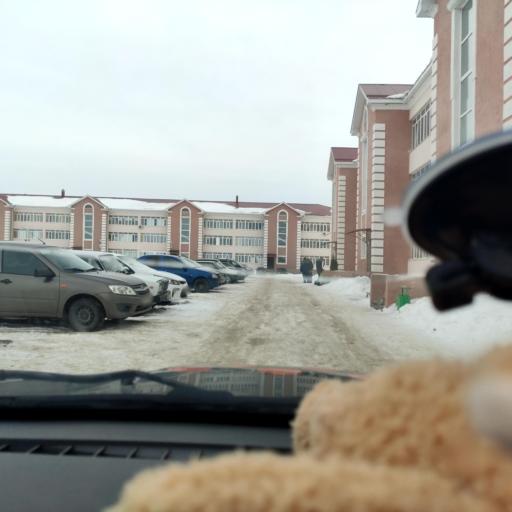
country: RU
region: Samara
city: Podstepki
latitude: 53.5293
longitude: 49.1814
